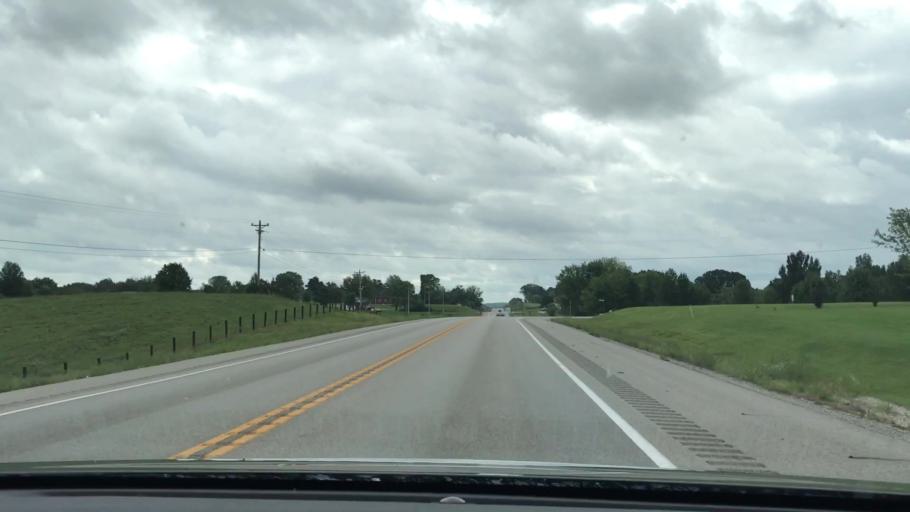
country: US
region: Kentucky
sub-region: Barren County
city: Glasgow
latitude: 36.9548
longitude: -85.8577
